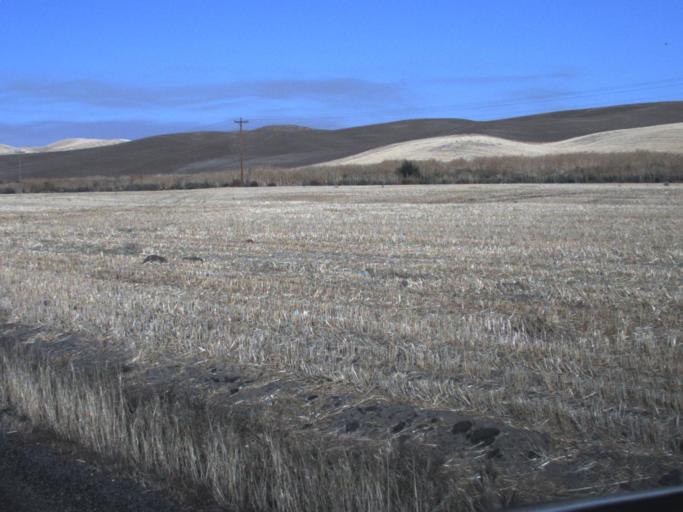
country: US
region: Washington
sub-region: Walla Walla County
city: Walla Walla
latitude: 46.1839
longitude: -118.3839
